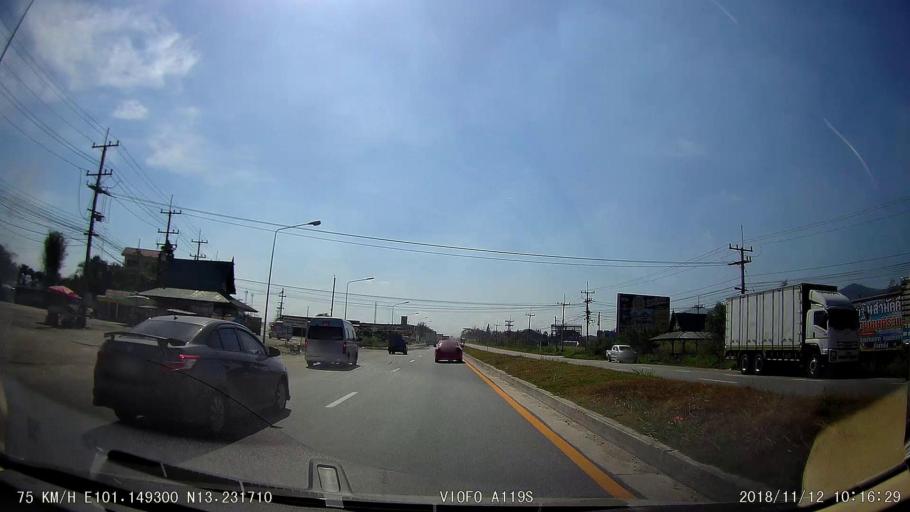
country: TH
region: Chon Buri
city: Ban Bueng
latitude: 13.2314
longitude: 101.1494
